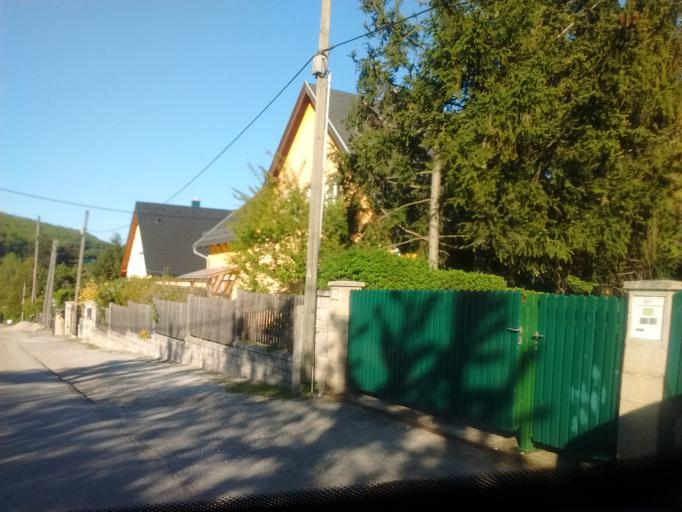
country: AT
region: Lower Austria
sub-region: Politischer Bezirk Modling
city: Giesshubl
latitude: 48.0791
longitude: 16.2134
